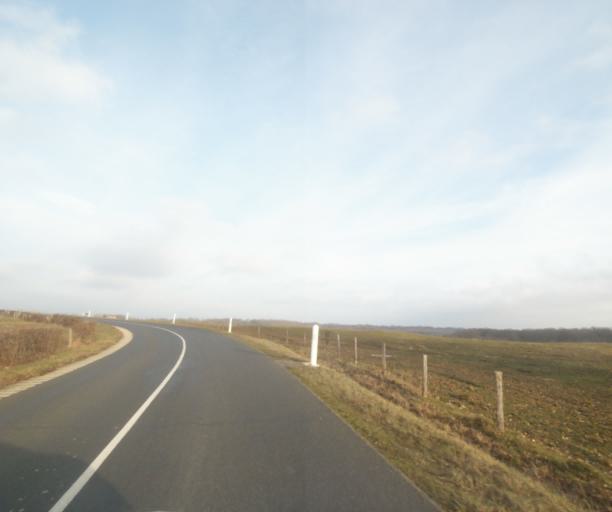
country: FR
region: Champagne-Ardenne
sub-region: Departement de la Marne
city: Sermaize-les-Bains
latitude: 48.7287
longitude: 4.9362
